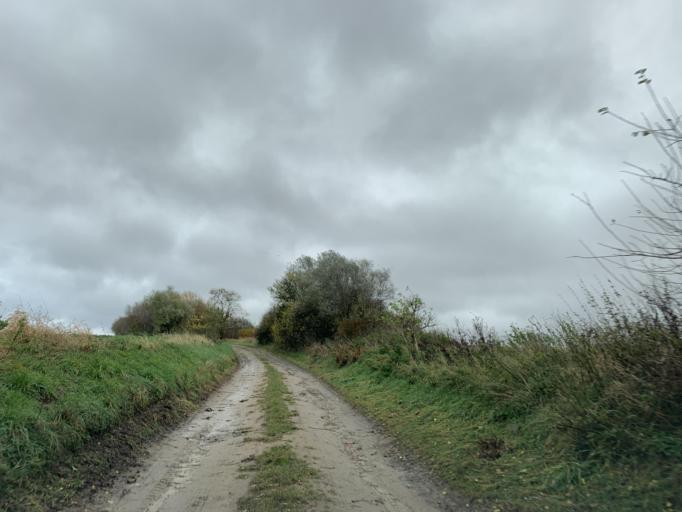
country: DE
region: Mecklenburg-Vorpommern
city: Blankensee
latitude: 53.3794
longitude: 13.2664
